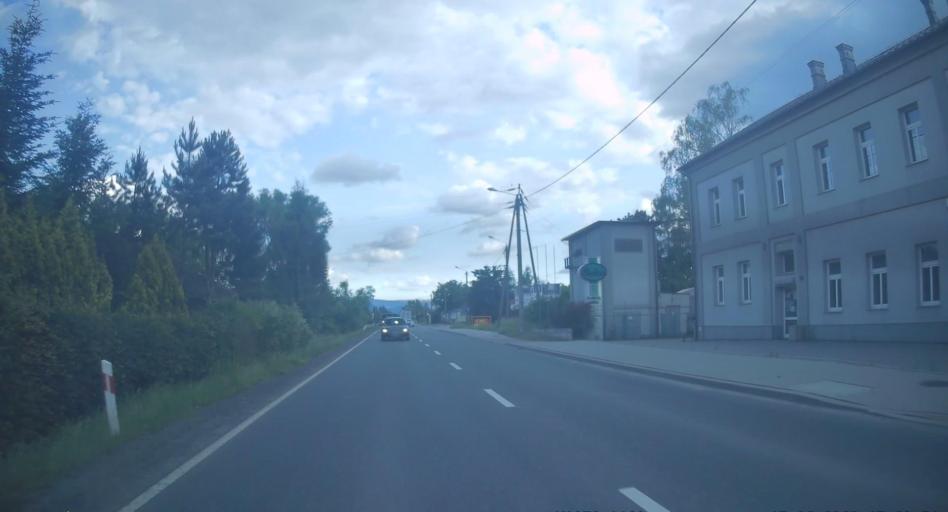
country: PL
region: Lesser Poland Voivodeship
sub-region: Powiat oswiecimski
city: Nowa Wies
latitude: 49.8986
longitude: 19.2180
